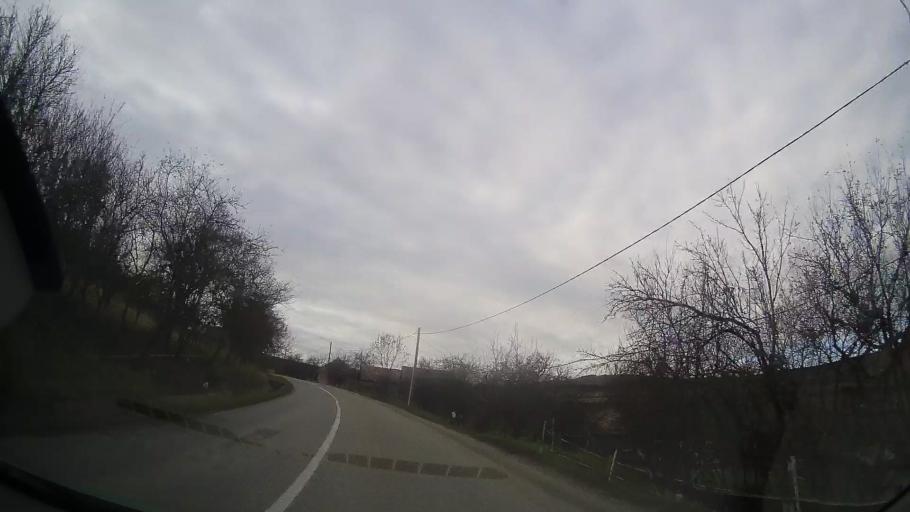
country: RO
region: Bistrita-Nasaud
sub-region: Comuna Budesti
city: Budesti
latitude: 46.8960
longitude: 24.2660
